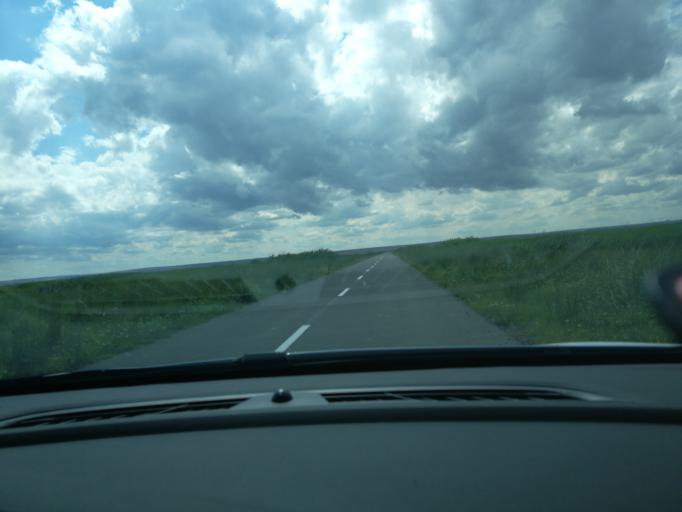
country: RO
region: Constanta
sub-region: Comuna Istria
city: Istria
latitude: 44.5376
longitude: 28.7485
